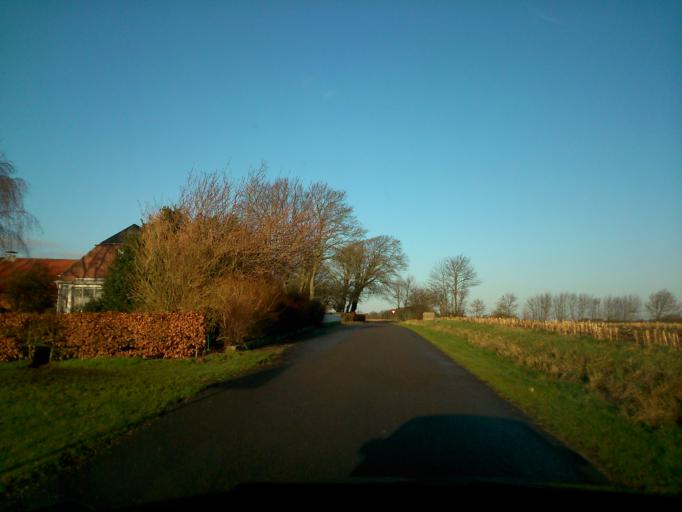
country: DK
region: Central Jutland
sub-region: Ringkobing-Skjern Kommune
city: Skjern
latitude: 55.9838
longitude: 8.5351
